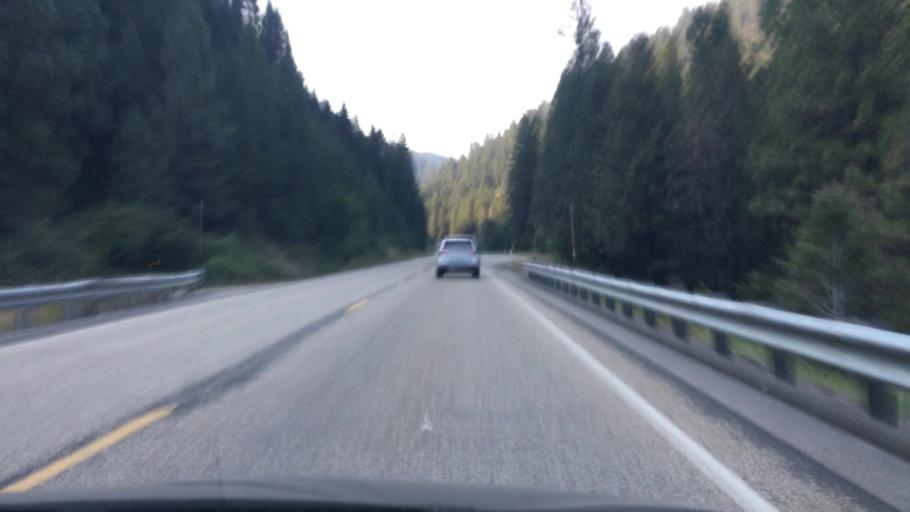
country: US
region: Idaho
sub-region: Valley County
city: Cascade
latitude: 44.1583
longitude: -116.1179
